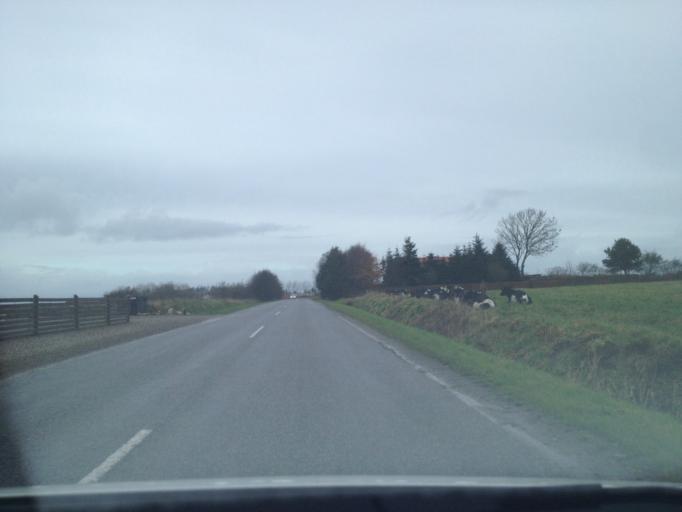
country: DK
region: South Denmark
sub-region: Tonder Kommune
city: Sherrebek
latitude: 55.2286
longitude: 8.8354
